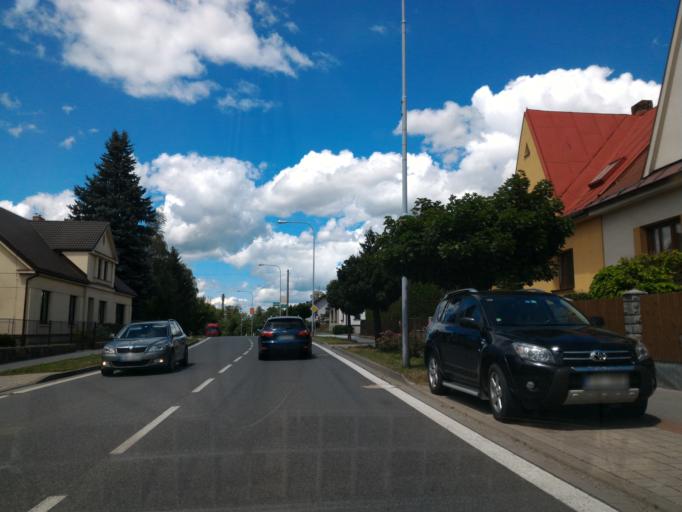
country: CZ
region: Vysocina
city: Zd'ar nad Sazavou Druhy
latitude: 49.5794
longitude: 15.9373
